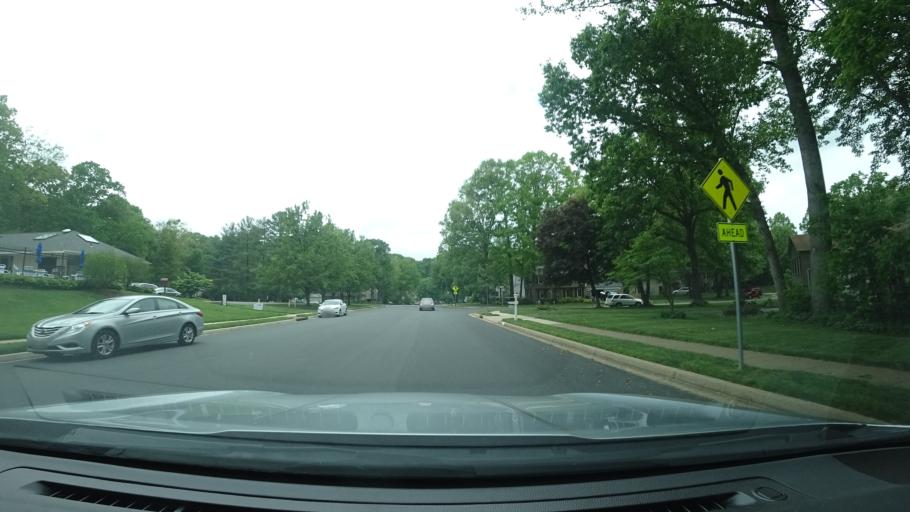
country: US
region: Virginia
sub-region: Fairfax County
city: Oak Hill
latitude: 38.9210
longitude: -77.3823
